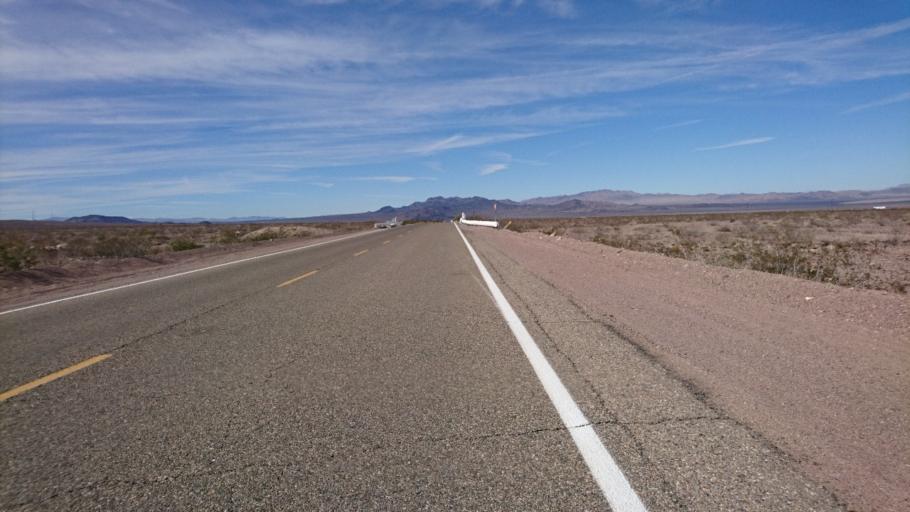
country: US
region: California
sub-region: San Bernardino County
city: Twentynine Palms
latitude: 34.7166
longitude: -116.1065
